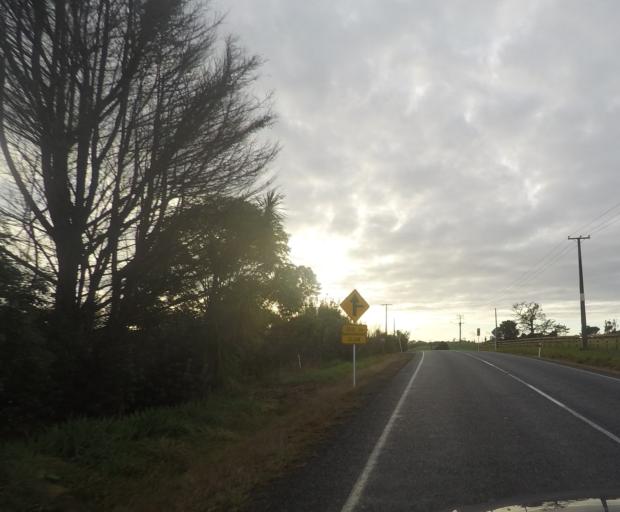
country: NZ
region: Auckland
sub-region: Auckland
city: Wellsford
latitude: -36.2223
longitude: 174.5746
